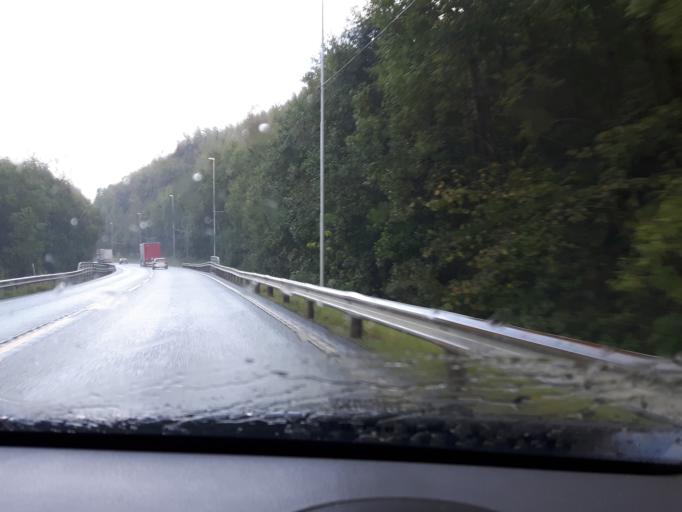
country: NO
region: Vest-Agder
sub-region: Sogne
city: Sogne
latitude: 58.0962
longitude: 7.7223
